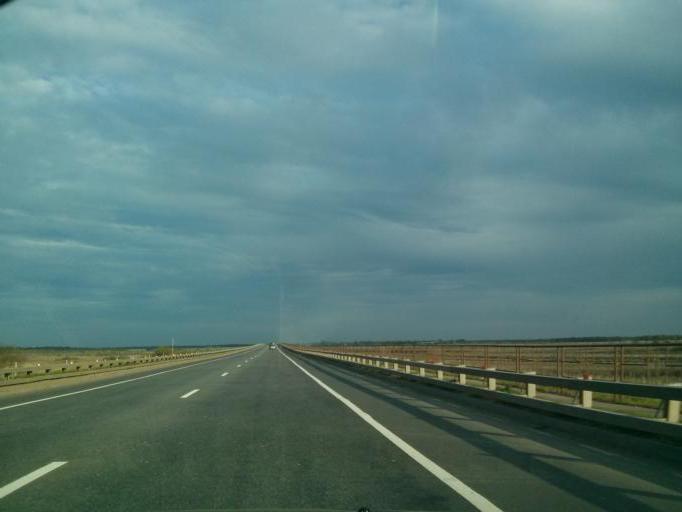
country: RU
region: Vladimir
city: Murom
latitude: 55.5986
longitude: 42.1040
